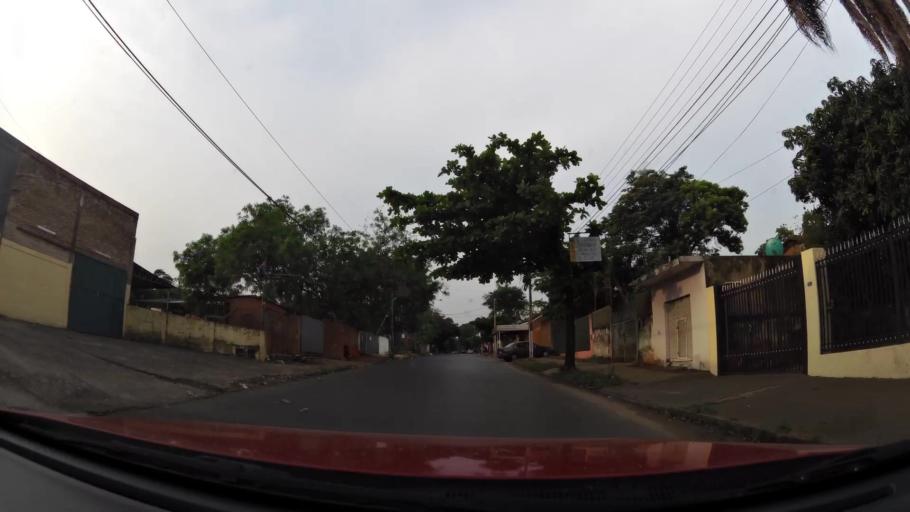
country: PY
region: Central
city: Lambare
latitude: -25.3237
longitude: -57.5743
